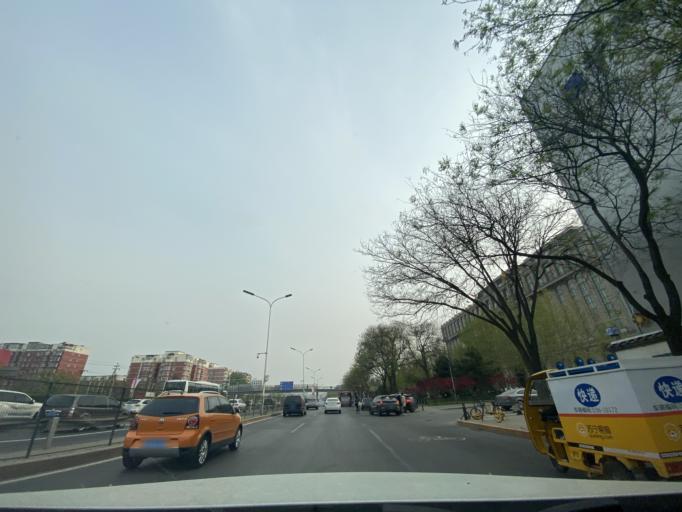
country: CN
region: Beijing
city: Sijiqing
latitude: 39.9366
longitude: 116.2679
